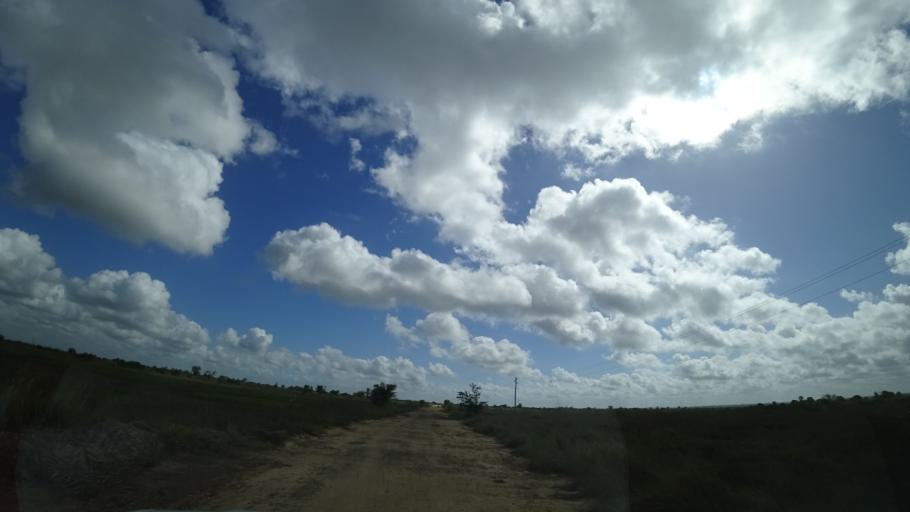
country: MZ
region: Sofala
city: Dondo
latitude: -19.4535
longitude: 34.5627
